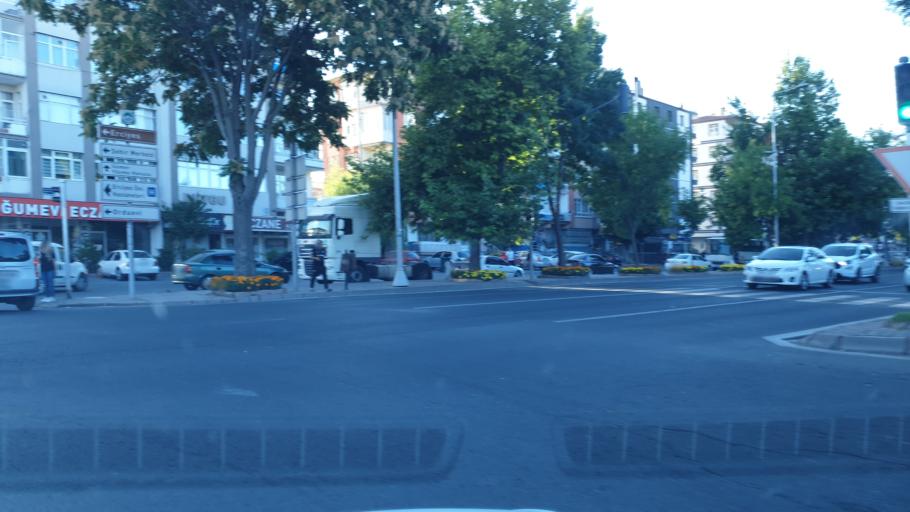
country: TR
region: Kayseri
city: Kayseri
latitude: 38.7396
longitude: 35.4913
